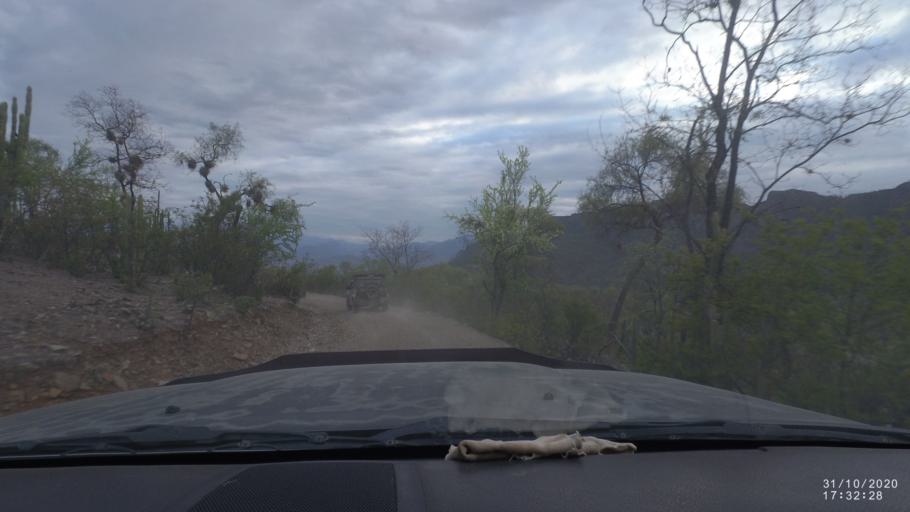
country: BO
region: Chuquisaca
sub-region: Provincia Zudanez
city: Mojocoya
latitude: -18.5992
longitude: -64.5533
